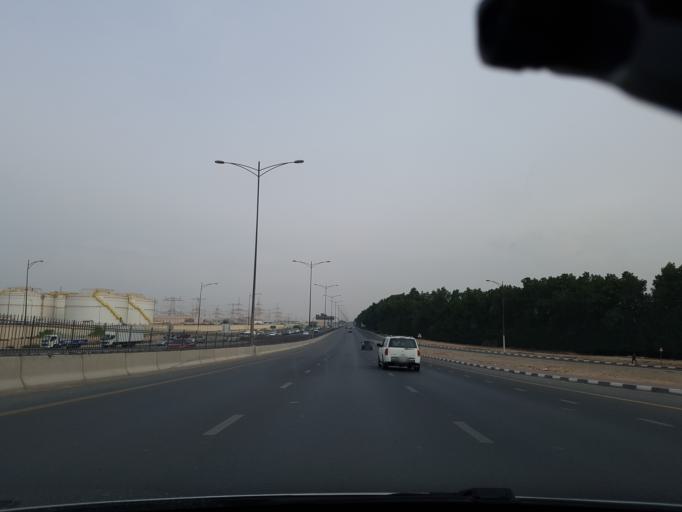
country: AE
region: Ajman
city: Ajman
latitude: 25.3719
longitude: 55.4567
